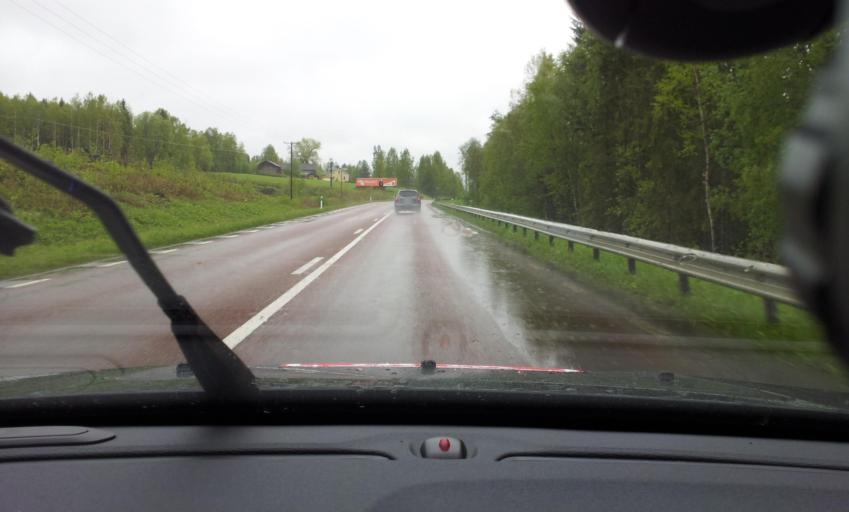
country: SE
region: Jaemtland
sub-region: Bergs Kommun
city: Hoverberg
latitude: 62.7732
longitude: 14.4452
